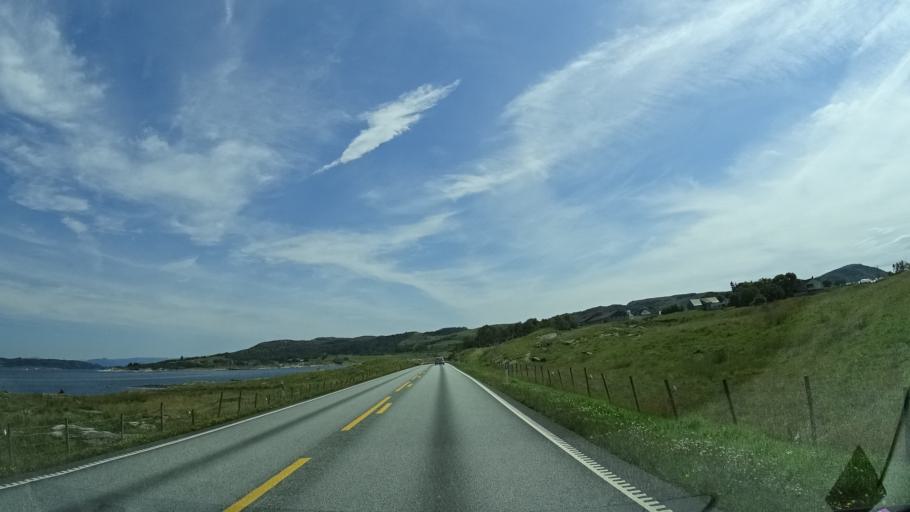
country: NO
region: Rogaland
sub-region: Rennesoy
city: Vikevag
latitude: 59.1214
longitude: 5.6843
